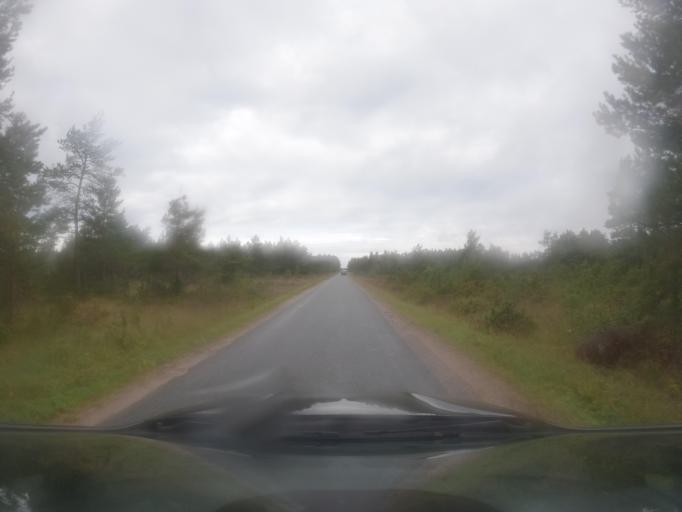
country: EE
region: Saare
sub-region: Kuressaare linn
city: Kuressaare
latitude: 58.4405
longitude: 21.9896
